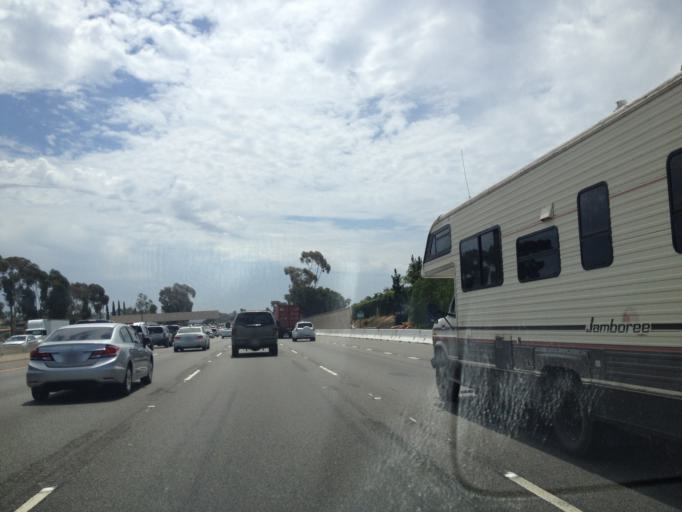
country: US
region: California
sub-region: Orange County
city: Dana Point
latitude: 33.4641
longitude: -117.6653
